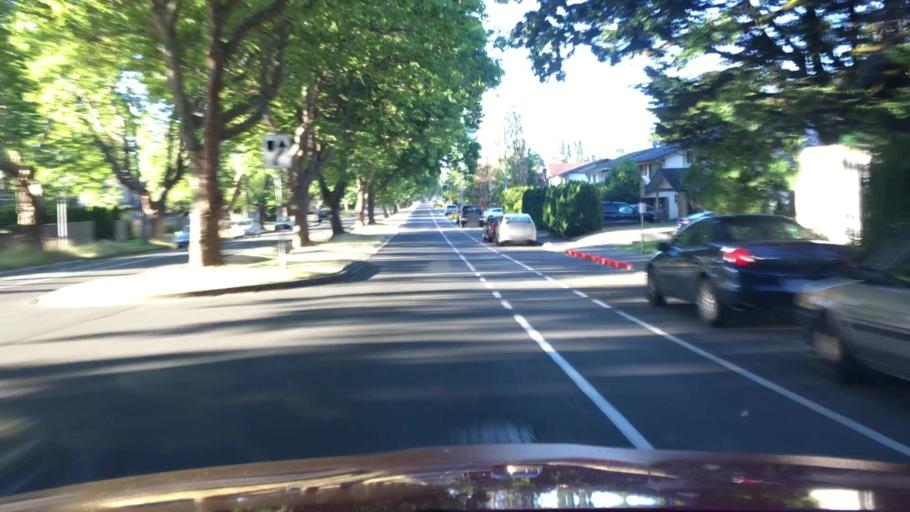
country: CA
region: British Columbia
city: Oak Bay
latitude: 48.4892
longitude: -123.3380
